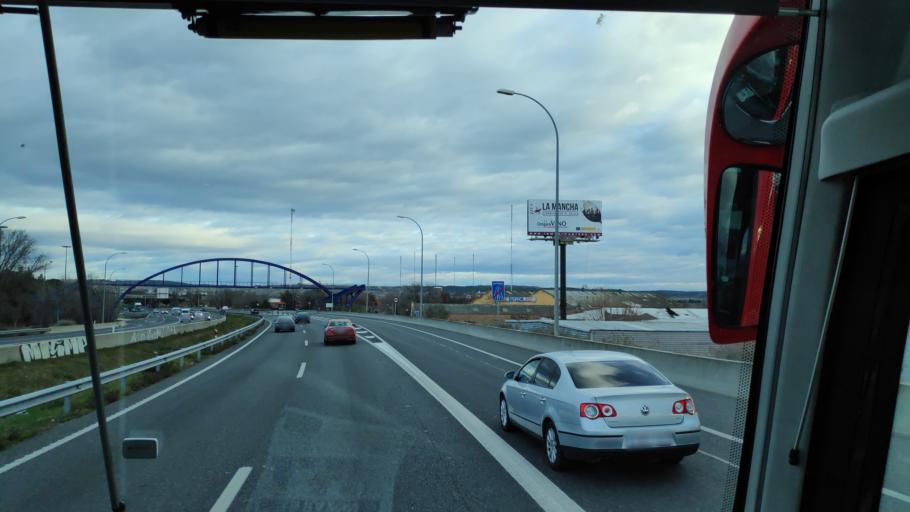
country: ES
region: Madrid
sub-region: Provincia de Madrid
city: Vaciamadrid
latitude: 40.3188
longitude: -3.5138
